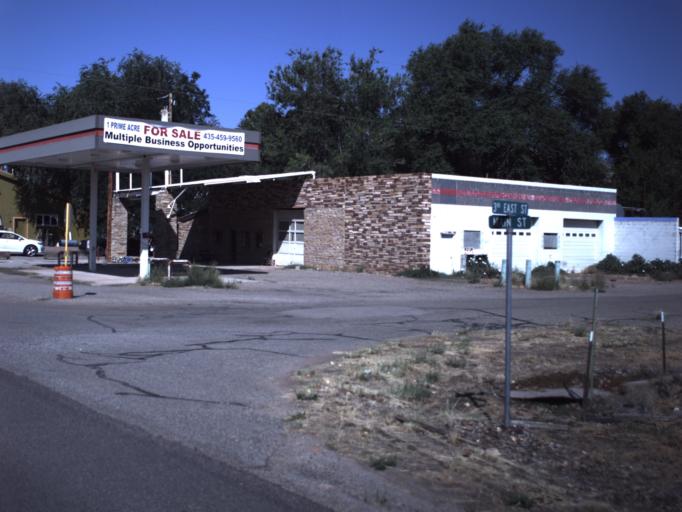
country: US
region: Utah
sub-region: San Juan County
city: Blanding
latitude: 37.2830
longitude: -109.5568
